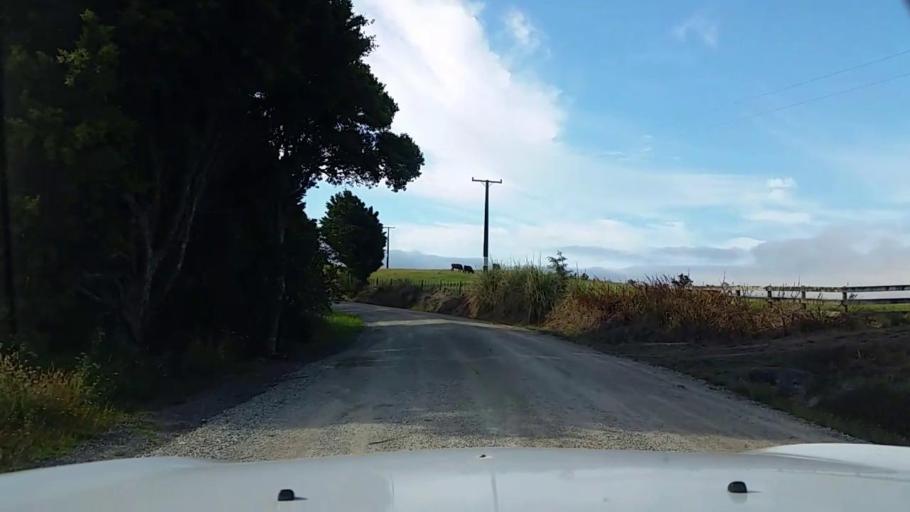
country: NZ
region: Northland
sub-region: Whangarei
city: Maungatapere
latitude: -35.6678
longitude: 174.1745
